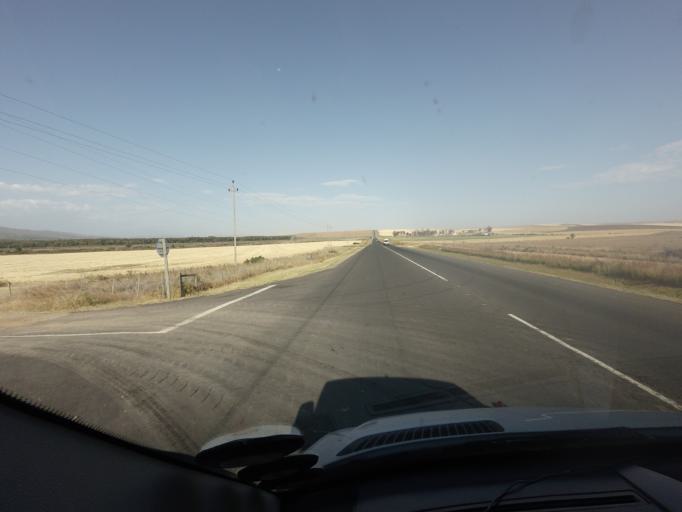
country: ZA
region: Western Cape
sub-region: Cape Winelands District Municipality
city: Ashton
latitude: -34.1543
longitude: 19.9294
